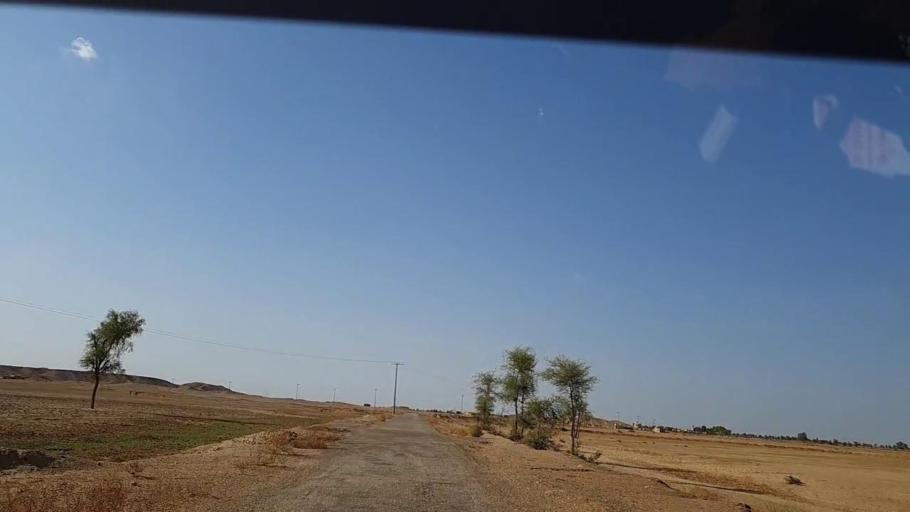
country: PK
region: Sindh
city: Johi
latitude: 26.5374
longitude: 67.5084
